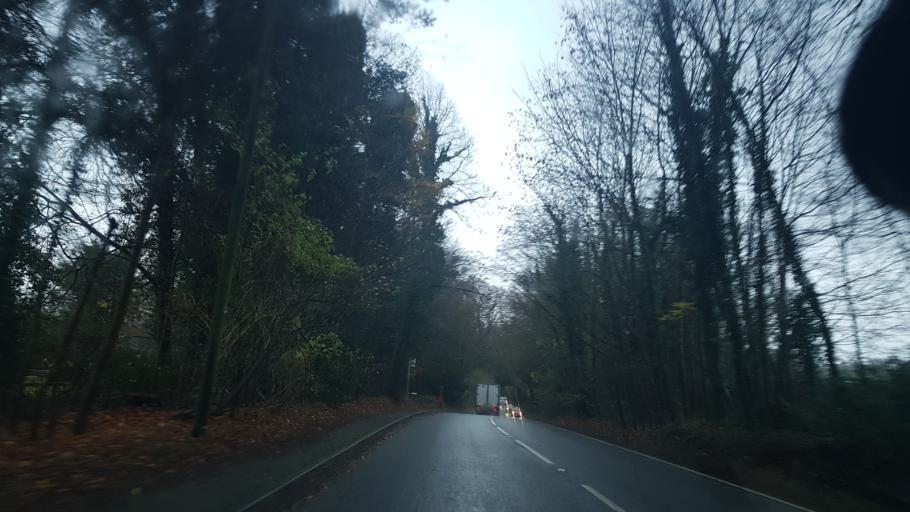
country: GB
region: England
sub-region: Surrey
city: East Horsley
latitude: 51.2624
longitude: -0.4114
